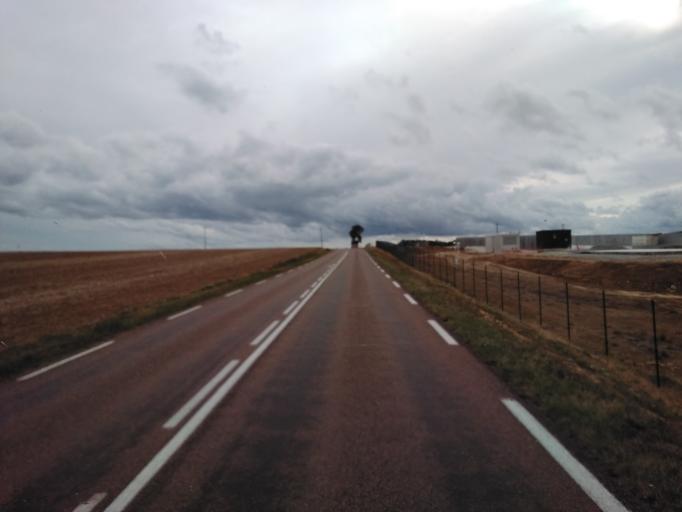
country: FR
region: Champagne-Ardenne
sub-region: Departement de l'Aube
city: Bar-sur-Seine
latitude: 48.1467
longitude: 4.4036
